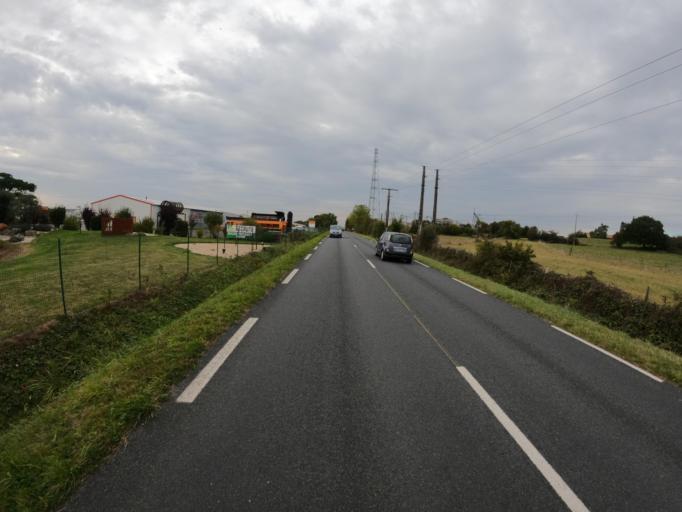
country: FR
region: Pays de la Loire
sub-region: Departement de la Loire-Atlantique
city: Getigne
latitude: 47.0755
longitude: -1.2324
